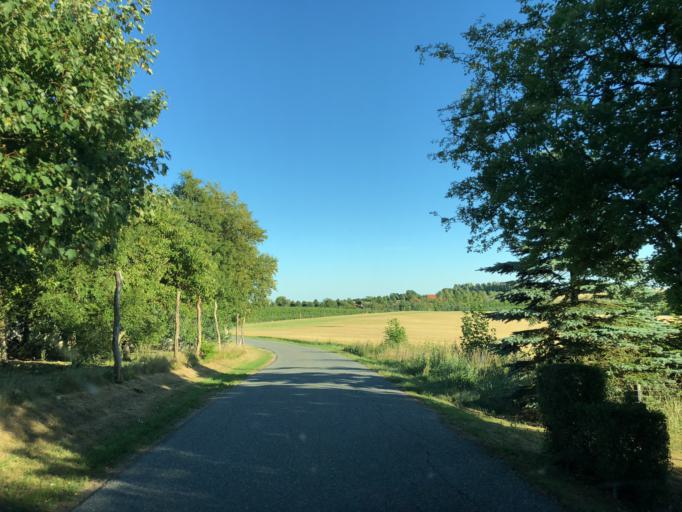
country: DK
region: Central Jutland
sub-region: Skanderborg Kommune
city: Ry
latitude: 55.9775
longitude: 9.8014
